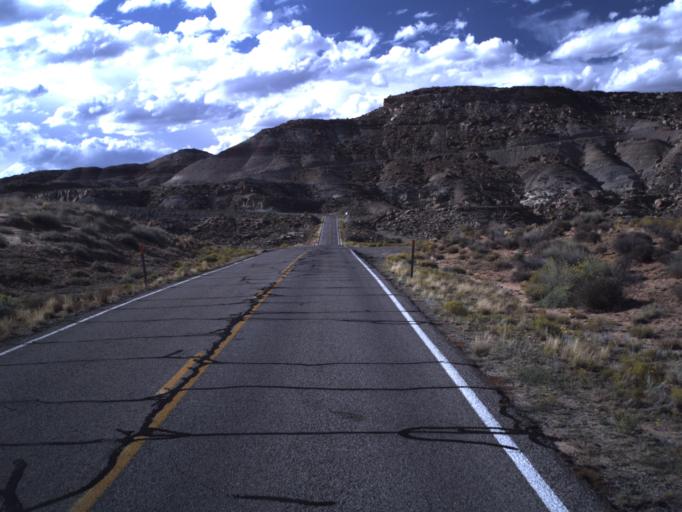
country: US
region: Utah
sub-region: San Juan County
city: Blanding
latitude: 37.3187
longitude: -109.3092
